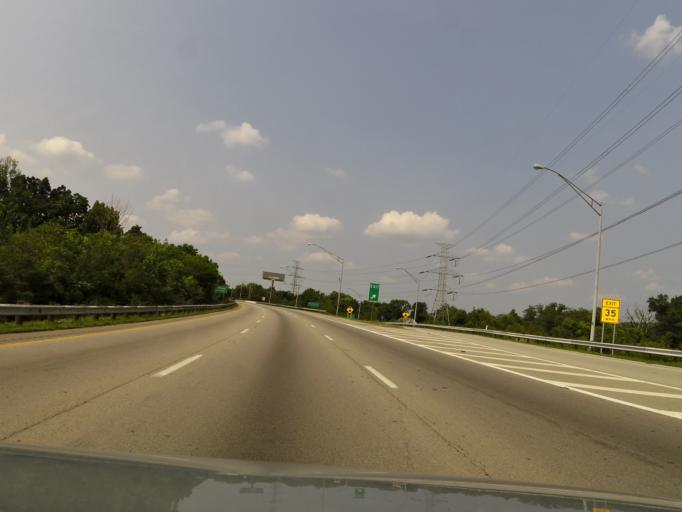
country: US
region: Ohio
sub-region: Hamilton County
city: Reading
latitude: 39.2184
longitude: -84.4492
